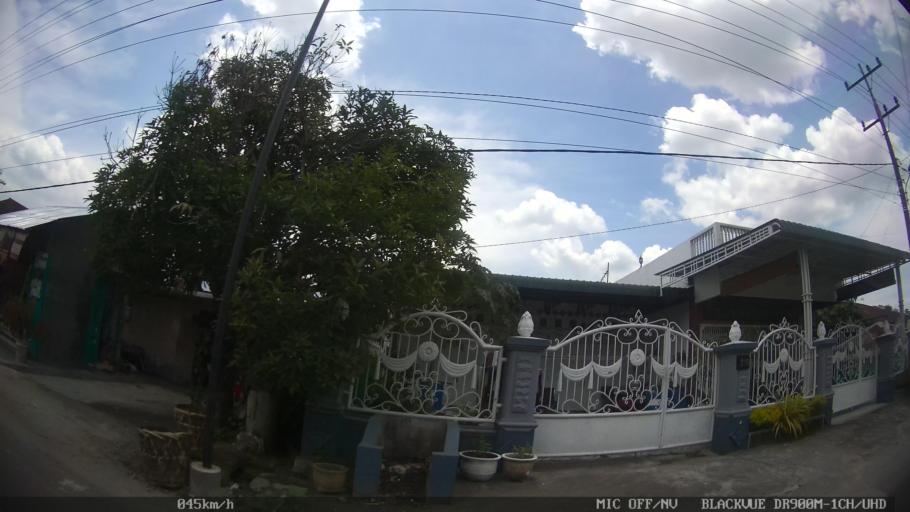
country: ID
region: North Sumatra
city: Binjai
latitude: 3.6279
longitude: 98.5134
